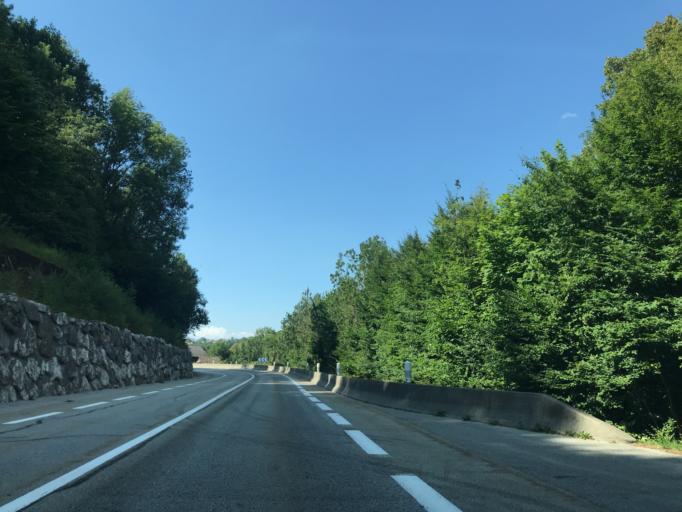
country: FR
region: Rhone-Alpes
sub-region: Departement de la Haute-Savoie
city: Dingy-Saint-Clair
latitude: 45.9160
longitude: 6.1980
